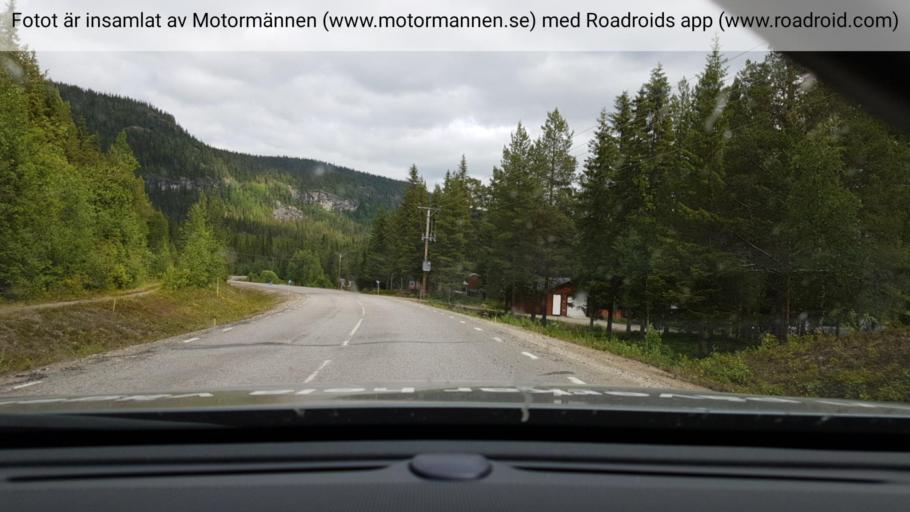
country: SE
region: Vaesterbotten
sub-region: Storumans Kommun
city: Fristad
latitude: 65.8075
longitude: 16.9092
